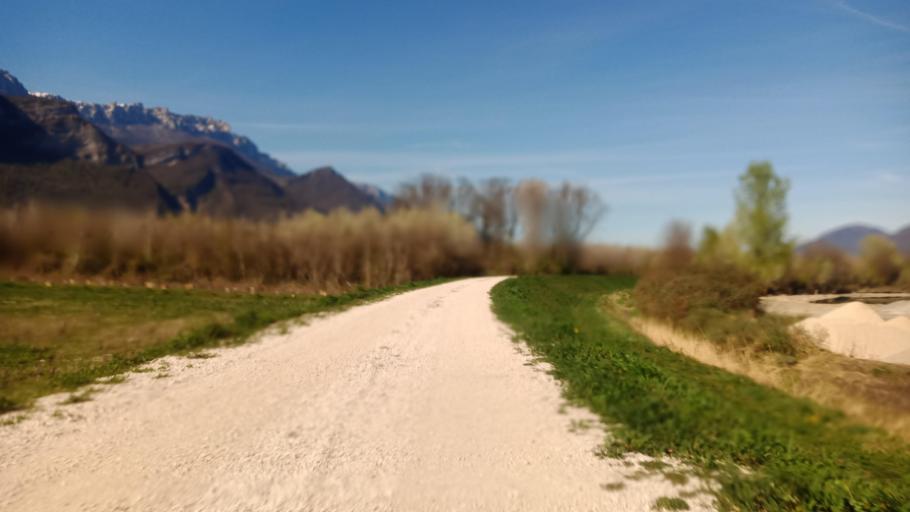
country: FR
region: Rhone-Alpes
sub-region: Departement de l'Isere
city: Froges
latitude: 45.2867
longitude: 5.9213
